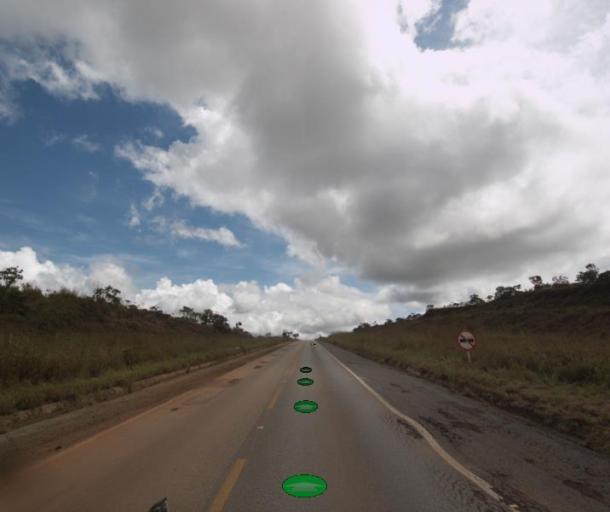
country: BR
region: Goias
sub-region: Pirenopolis
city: Pirenopolis
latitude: -15.7771
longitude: -48.5007
